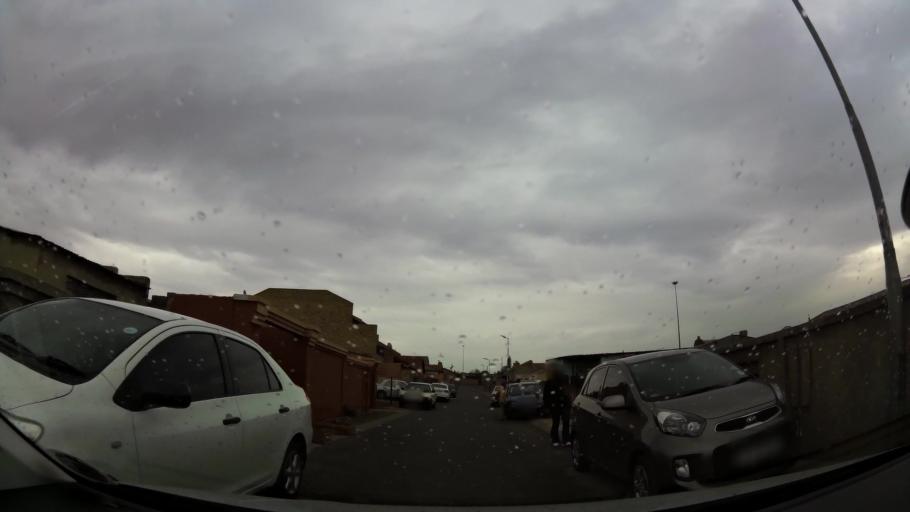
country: ZA
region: Gauteng
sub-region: City of Johannesburg Metropolitan Municipality
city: Soweto
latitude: -26.2510
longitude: 27.8661
